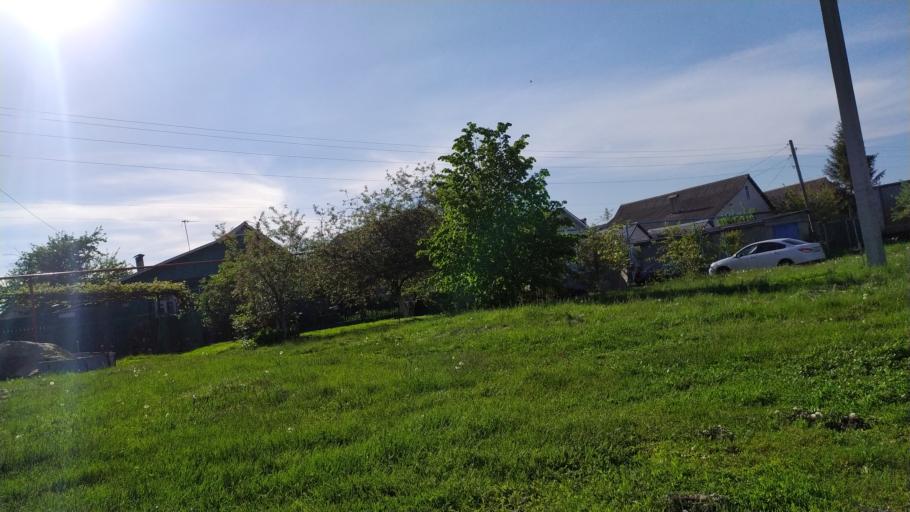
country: RU
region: Kursk
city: Kursk
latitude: 51.6358
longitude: 36.1495
